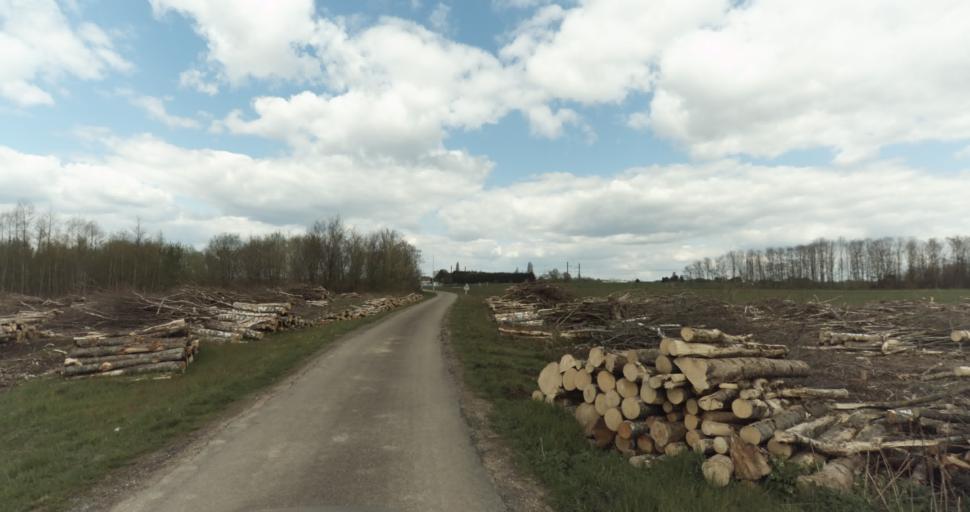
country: FR
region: Bourgogne
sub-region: Departement de la Cote-d'Or
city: Auxonne
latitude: 47.1709
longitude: 5.3945
